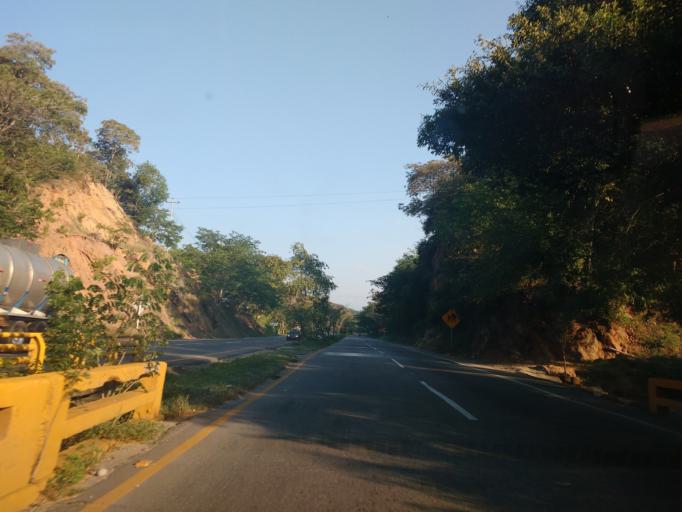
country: CO
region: Cundinamarca
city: Ricaurte
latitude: 4.2481
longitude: -74.7248
